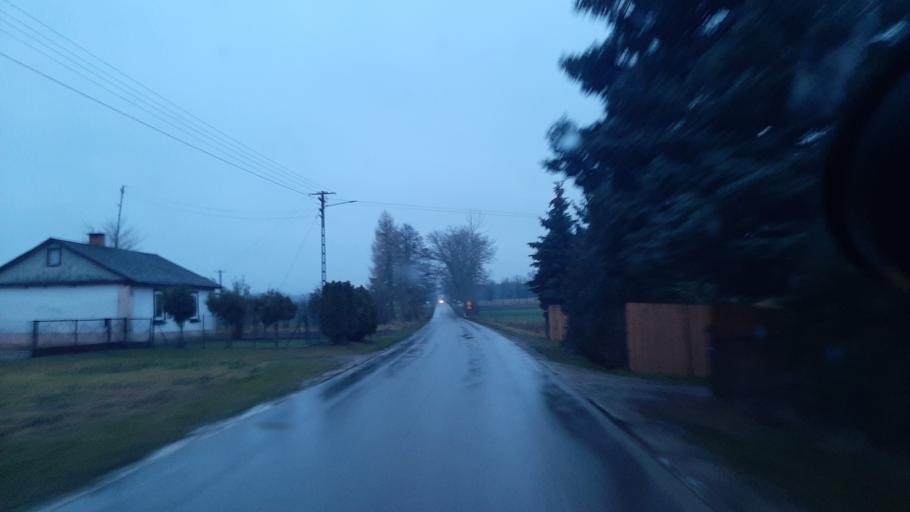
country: PL
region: Lublin Voivodeship
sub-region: Powiat lubartowski
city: Kamionka
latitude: 51.4017
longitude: 22.4129
